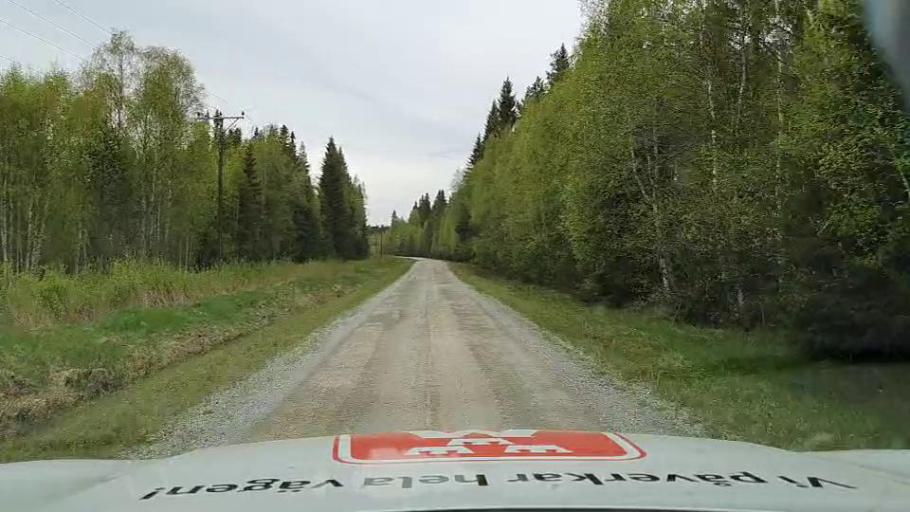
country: SE
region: Jaemtland
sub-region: Bergs Kommun
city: Hoverberg
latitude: 62.6799
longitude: 14.7986
